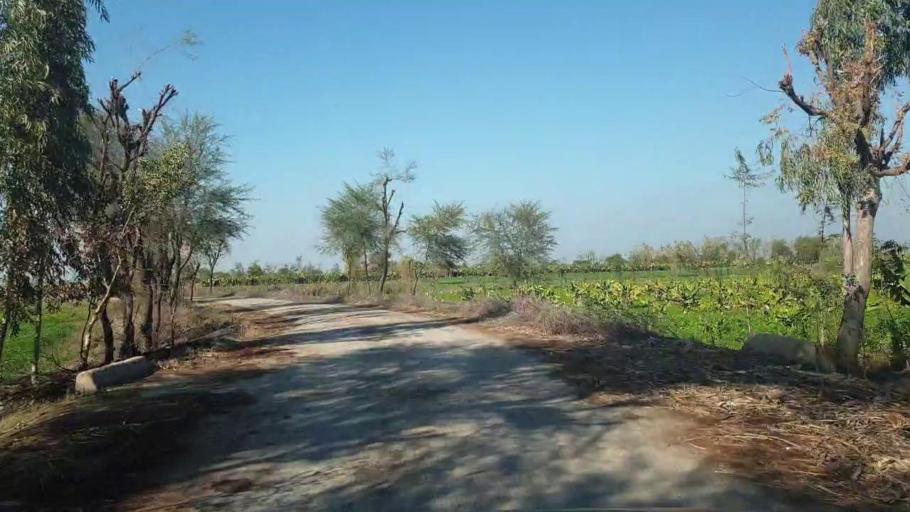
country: PK
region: Sindh
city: Shahdadpur
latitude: 25.9115
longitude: 68.5344
